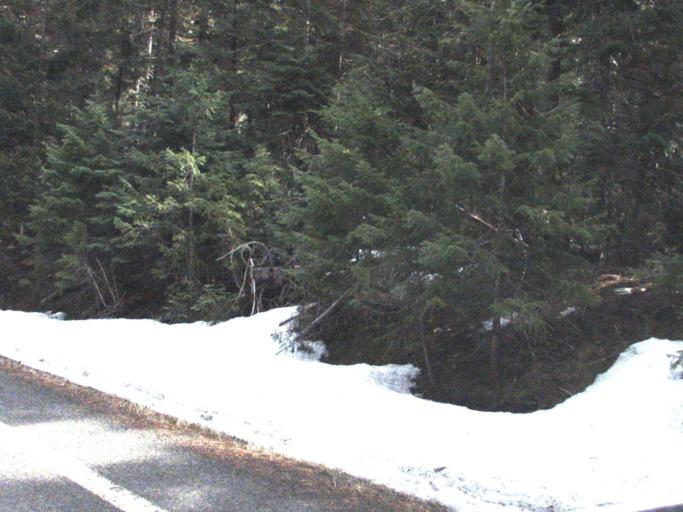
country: US
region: Washington
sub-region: Kittitas County
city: Cle Elum
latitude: 46.9784
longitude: -121.1559
